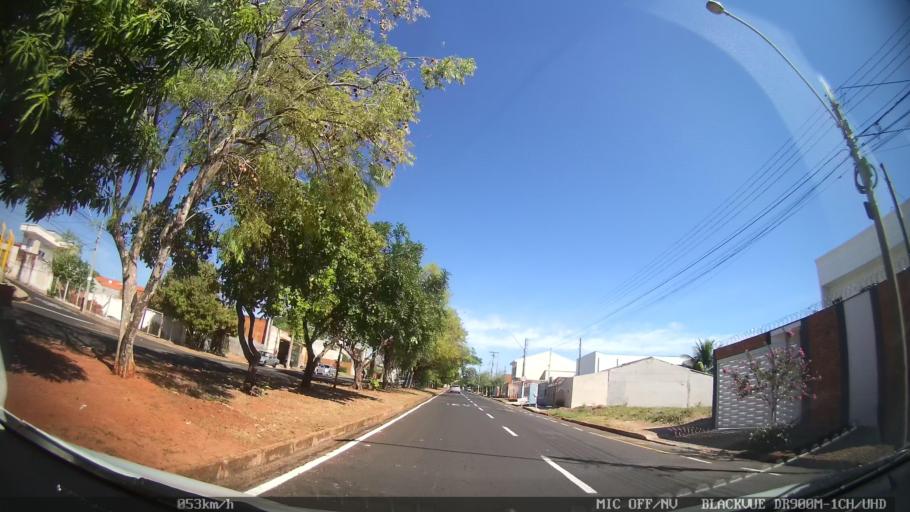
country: BR
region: Sao Paulo
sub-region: Sao Jose Do Rio Preto
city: Sao Jose do Rio Preto
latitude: -20.7664
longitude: -49.4064
